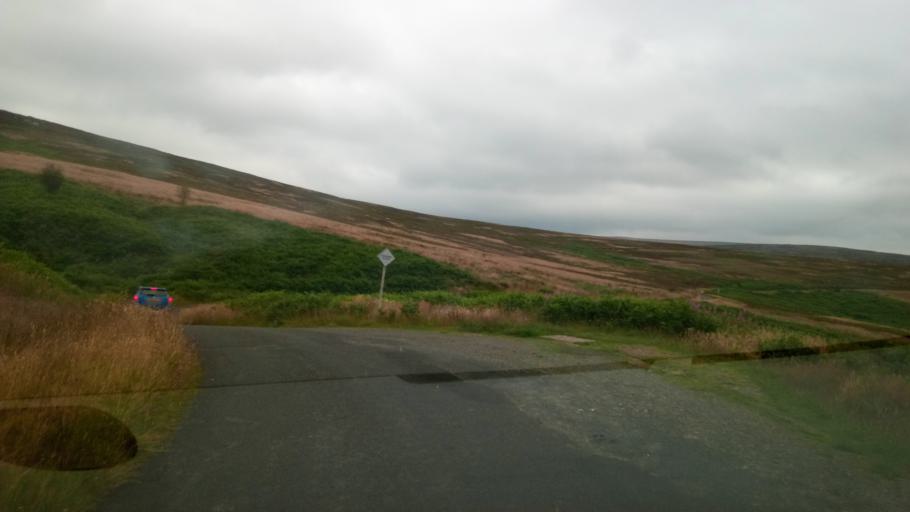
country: GB
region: Scotland
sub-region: Dumfries and Galloway
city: Langholm
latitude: 55.1690
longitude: -2.9574
